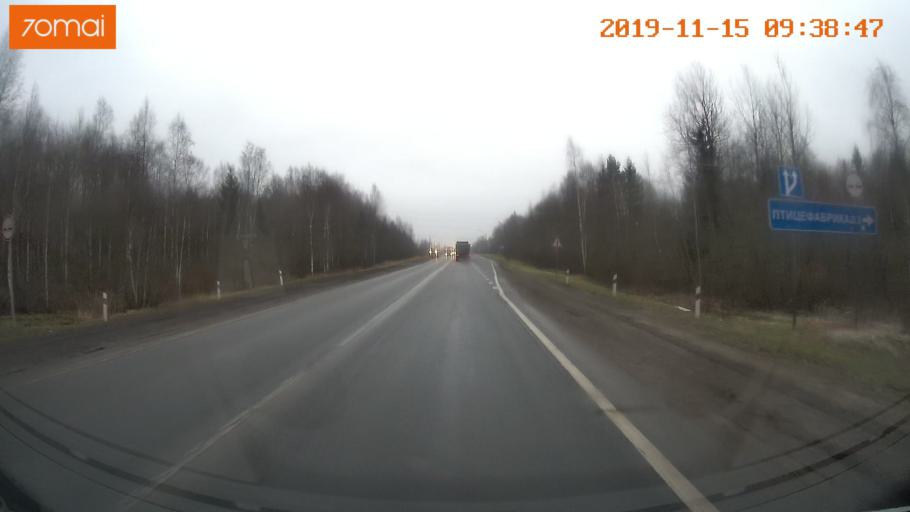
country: RU
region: Vologda
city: Sheksna
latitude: 59.2290
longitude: 38.4616
